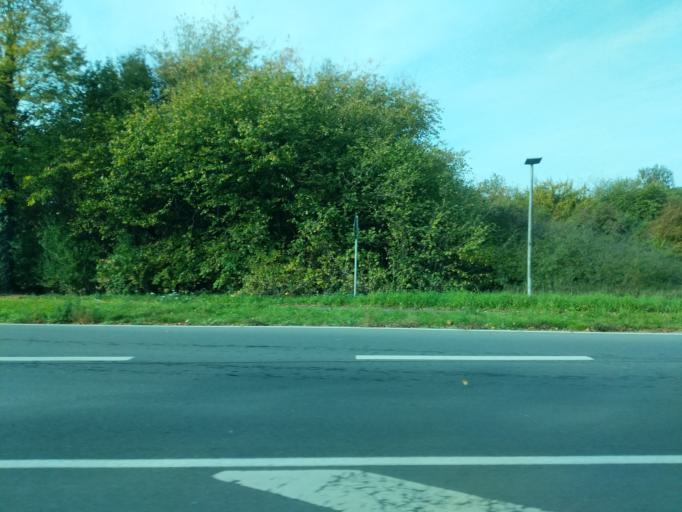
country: DE
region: Schleswig-Holstein
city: Lagerdorf
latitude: 53.8729
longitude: 9.5894
